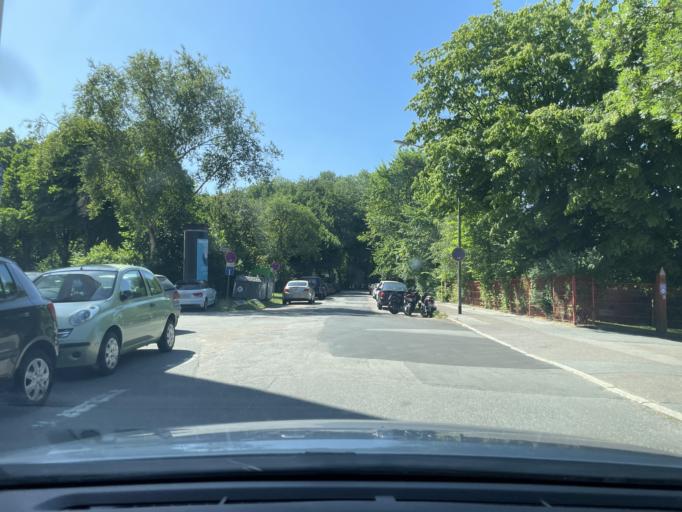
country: DE
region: Schleswig-Holstein
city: Flensburg
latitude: 54.7779
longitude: 9.4403
